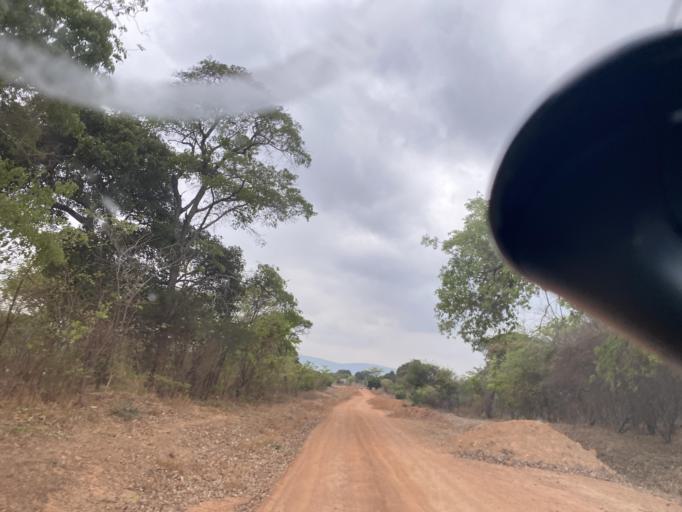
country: ZM
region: Lusaka
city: Chongwe
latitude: -15.2397
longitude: 28.7187
